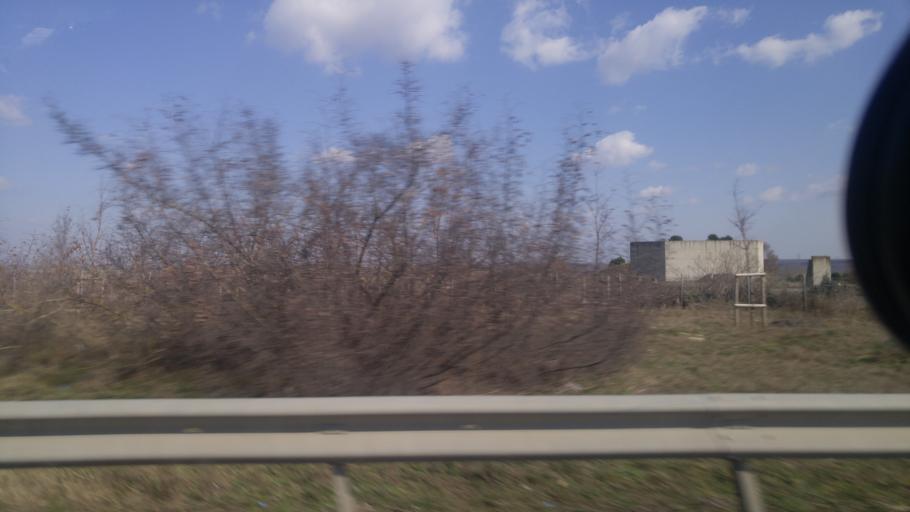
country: TR
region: Istanbul
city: Buyukcavuslu
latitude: 41.1950
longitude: 28.0852
